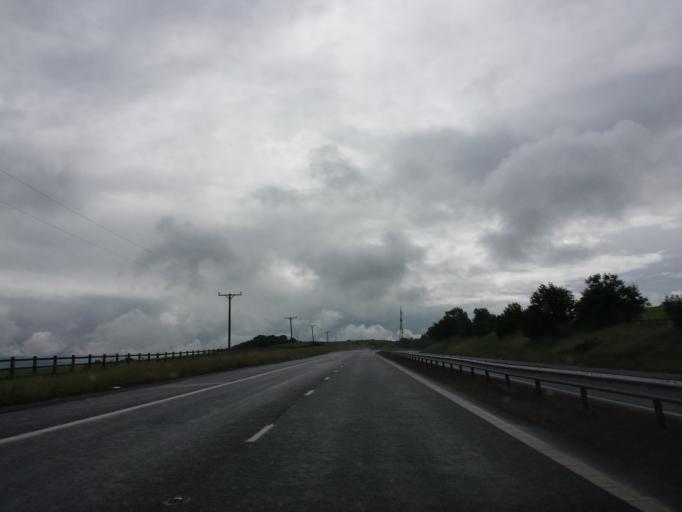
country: GB
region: Scotland
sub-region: Perth and Kinross
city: Perth
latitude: 56.3790
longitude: -3.4539
